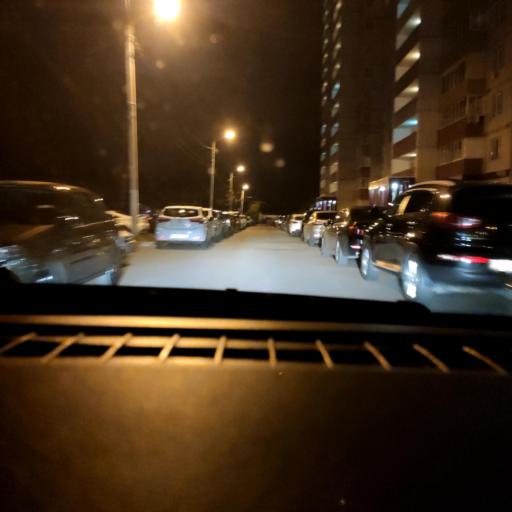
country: RU
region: Voronezj
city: Voronezh
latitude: 51.7121
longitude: 39.2017
